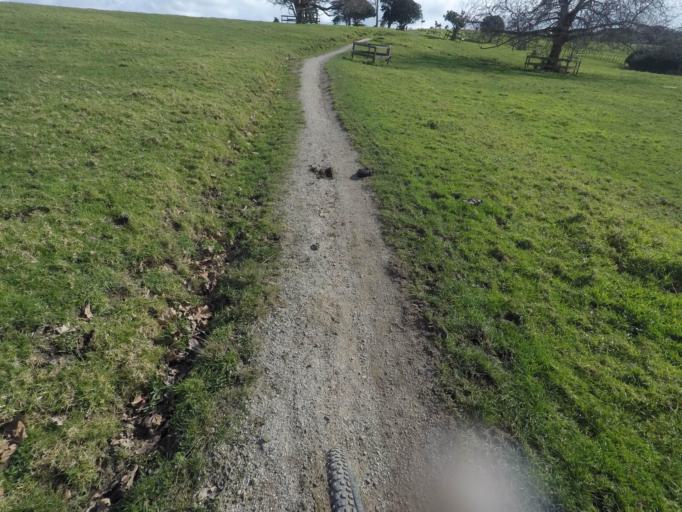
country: NZ
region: Auckland
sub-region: Auckland
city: Manukau City
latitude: -36.9924
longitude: 174.9059
